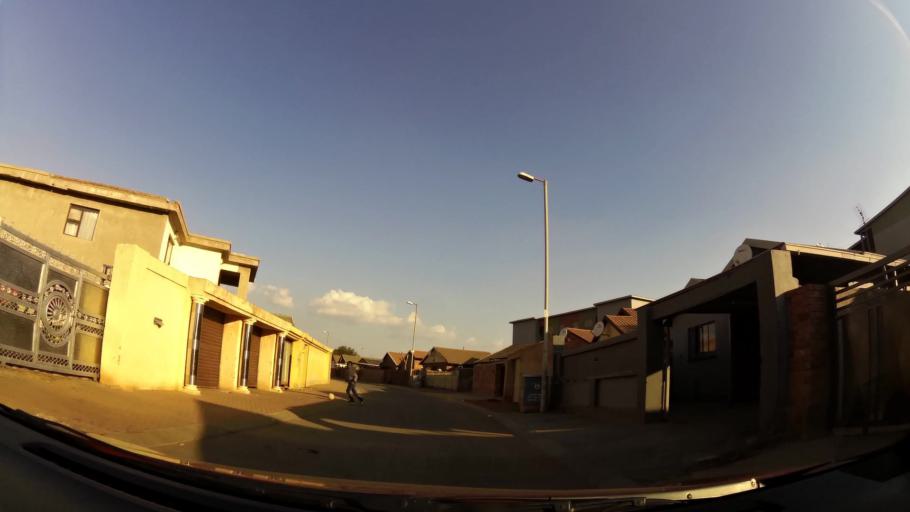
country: ZA
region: Gauteng
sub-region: City of Johannesburg Metropolitan Municipality
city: Soweto
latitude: -26.2283
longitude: 27.8563
